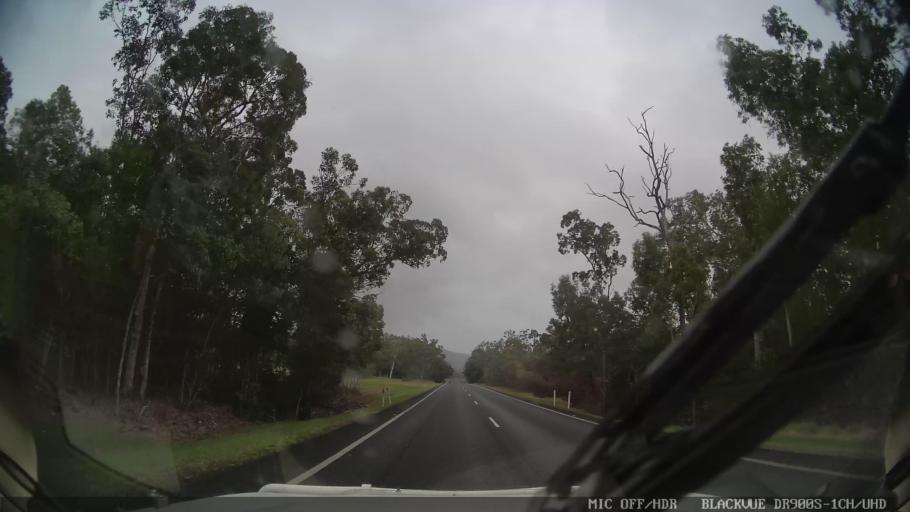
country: AU
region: Queensland
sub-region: Hinchinbrook
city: Ingham
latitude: -18.4437
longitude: 146.1405
